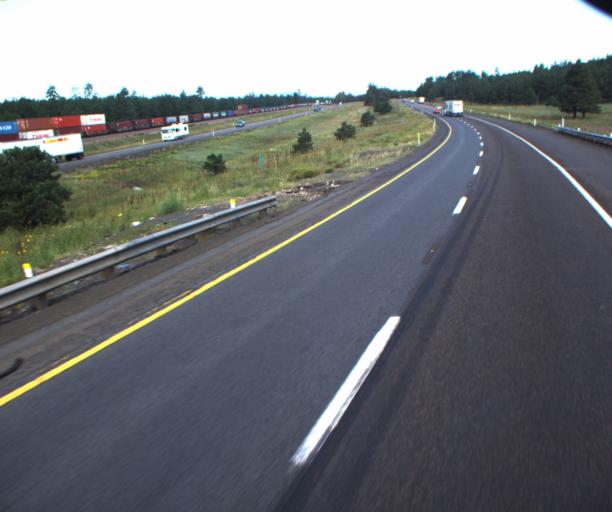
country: US
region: Arizona
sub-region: Coconino County
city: Flagstaff
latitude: 35.2126
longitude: -111.7750
